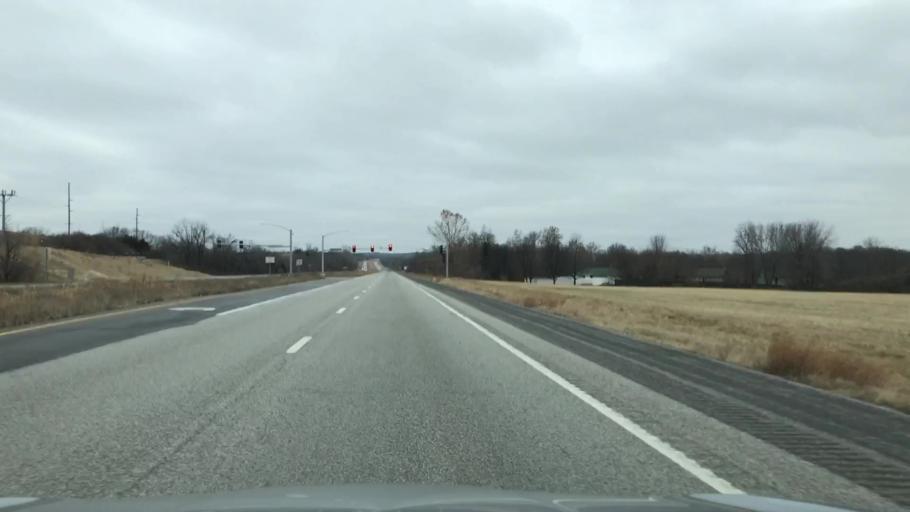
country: US
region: Missouri
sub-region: Clay County
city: Liberty
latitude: 39.2049
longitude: -94.4040
